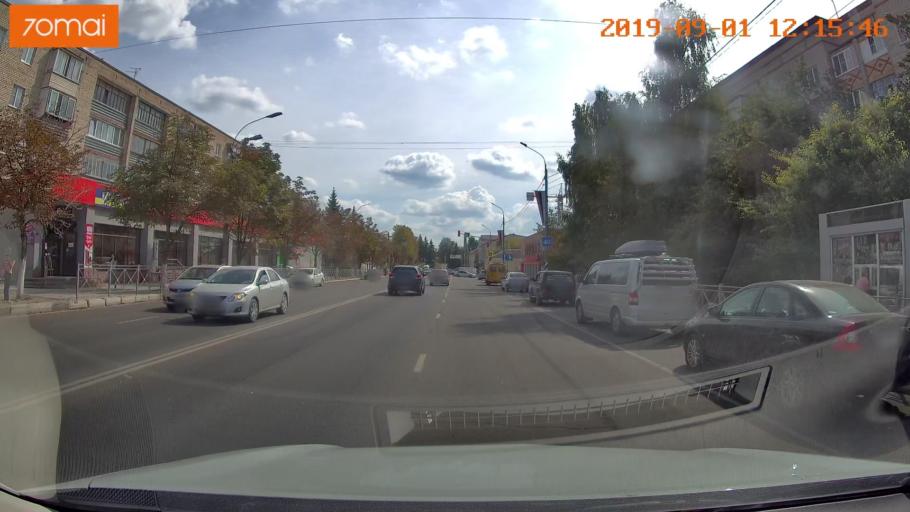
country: RU
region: Kaluga
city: Maloyaroslavets
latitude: 55.0112
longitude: 36.4639
